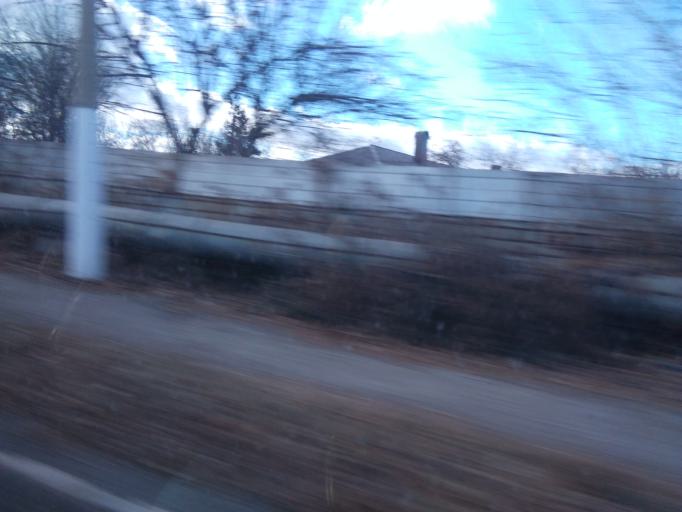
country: RU
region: Chelyabinsk
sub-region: Gorod Magnitogorsk
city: Magnitogorsk
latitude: 53.3942
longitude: 59.0506
